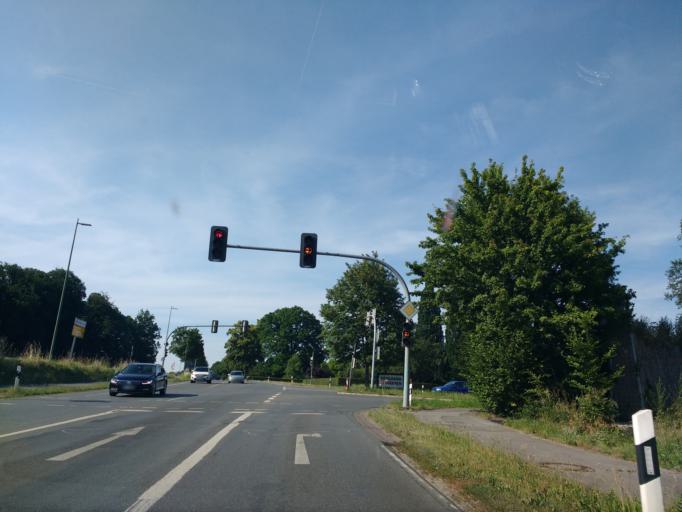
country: DE
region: North Rhine-Westphalia
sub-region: Regierungsbezirk Detmold
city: Bielefeld
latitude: 52.0623
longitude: 8.5561
